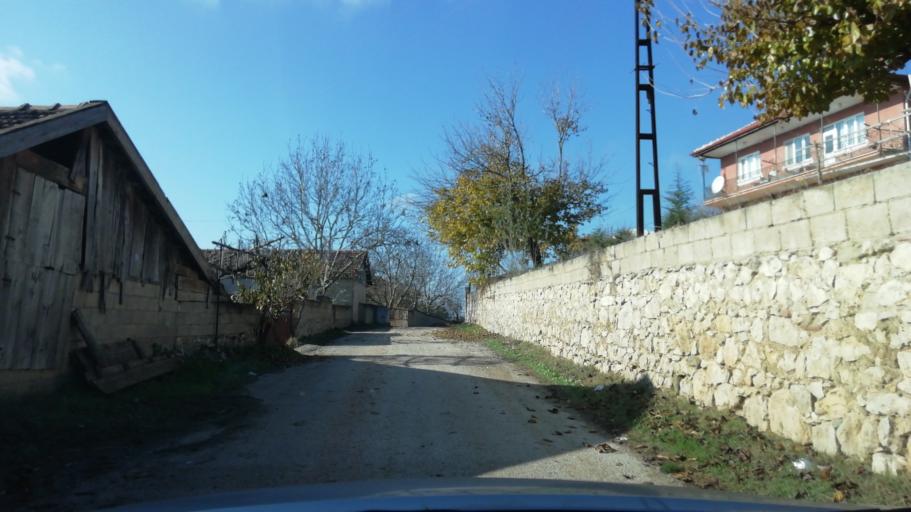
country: TR
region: Karabuk
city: Safranbolu
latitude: 41.2297
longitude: 32.7842
